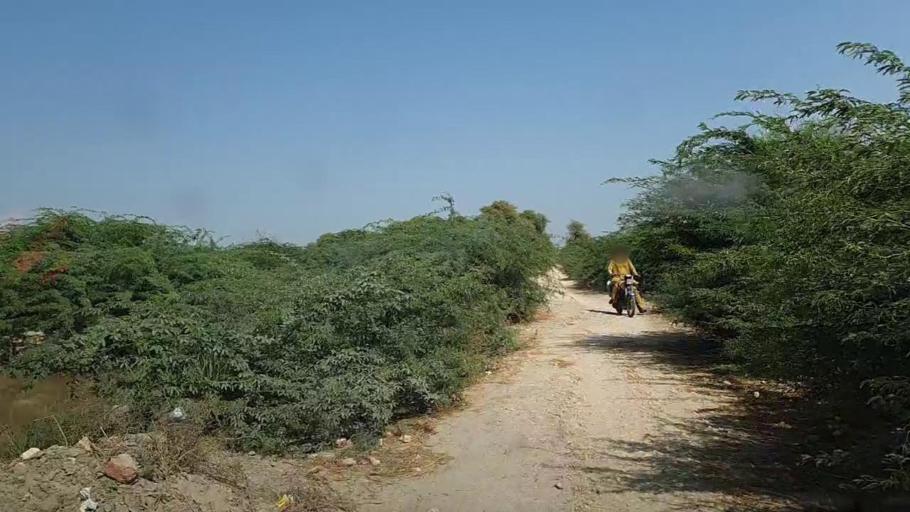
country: PK
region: Sindh
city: Mirpur Batoro
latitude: 24.7133
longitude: 68.4315
